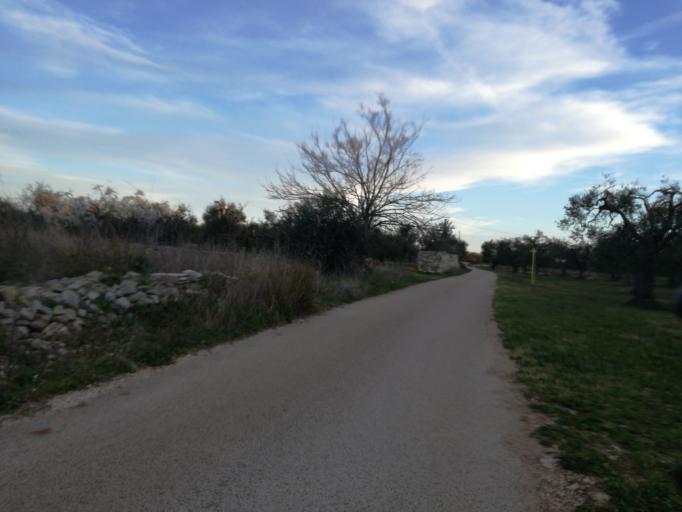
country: IT
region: Apulia
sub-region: Provincia di Bari
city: Lamie
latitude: 41.0207
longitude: 16.8720
